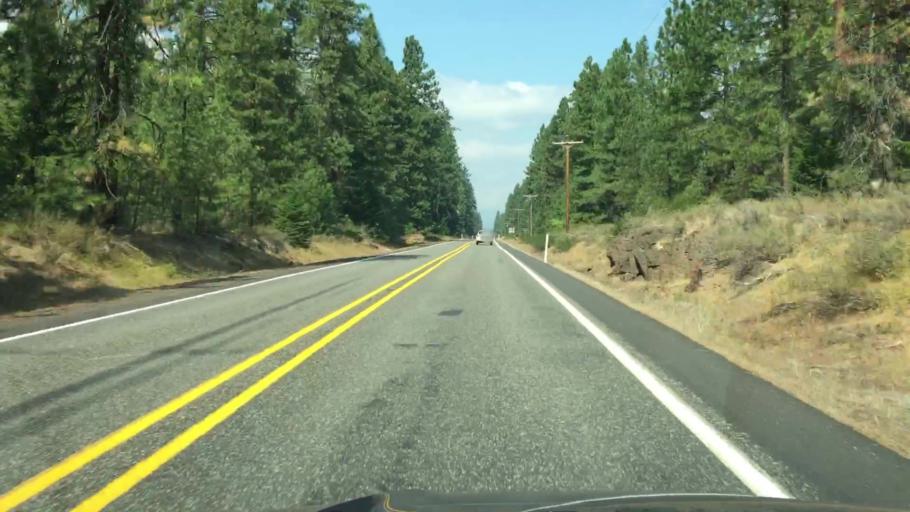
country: US
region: Washington
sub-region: Klickitat County
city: White Salmon
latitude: 45.9699
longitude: -121.4951
